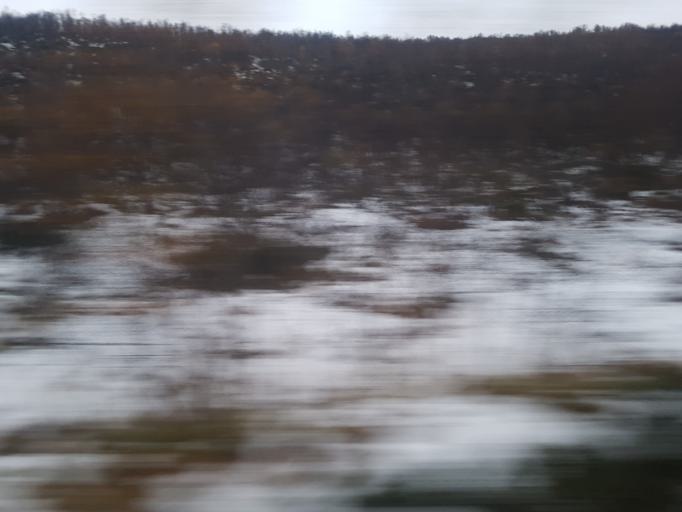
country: NO
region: Sor-Trondelag
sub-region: Oppdal
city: Oppdal
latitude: 62.3328
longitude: 9.6212
